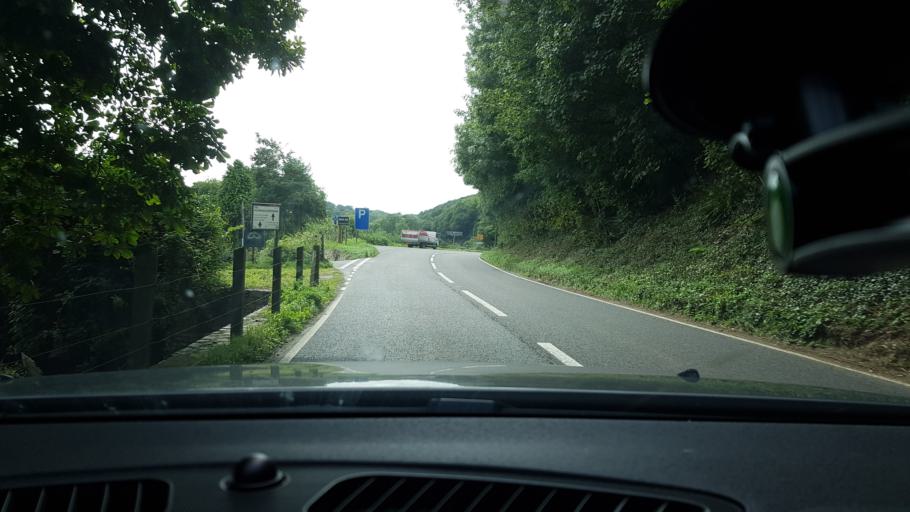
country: GB
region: England
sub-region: Cornwall
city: Camelford
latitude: 50.5782
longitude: -4.7362
